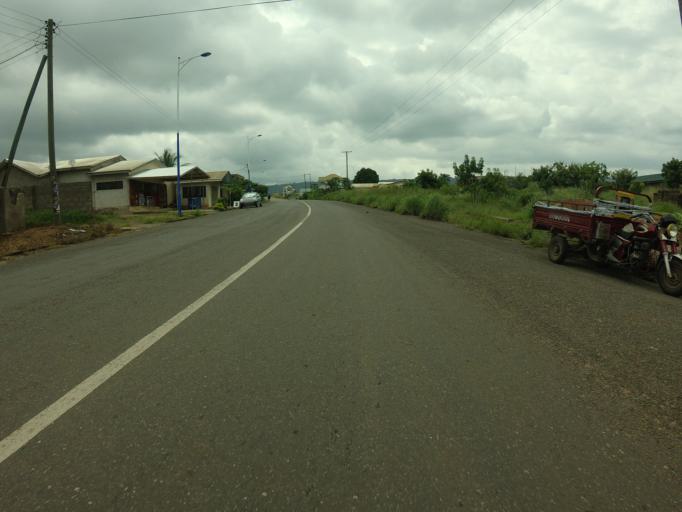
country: GH
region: Volta
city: Ho
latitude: 6.6219
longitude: 0.4948
